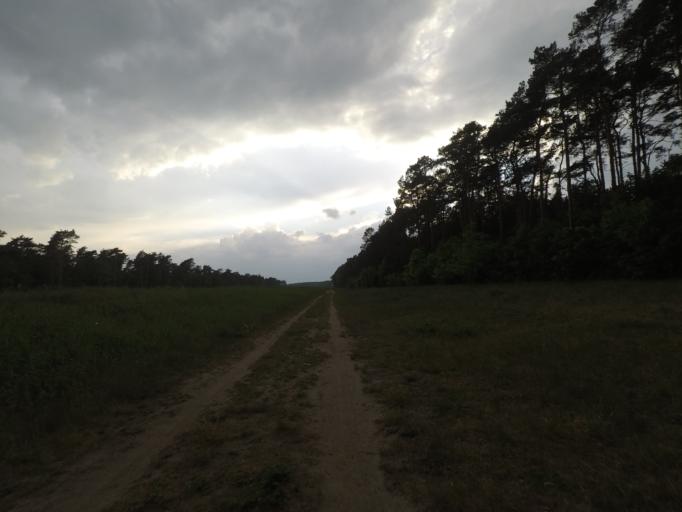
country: DE
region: Brandenburg
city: Melchow
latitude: 52.8597
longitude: 13.7178
